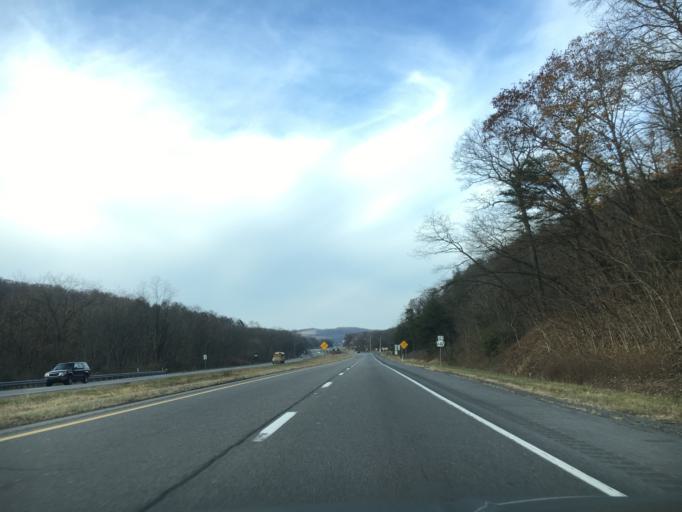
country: US
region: Pennsylvania
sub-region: Montour County
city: Danville
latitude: 40.9793
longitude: -76.6247
